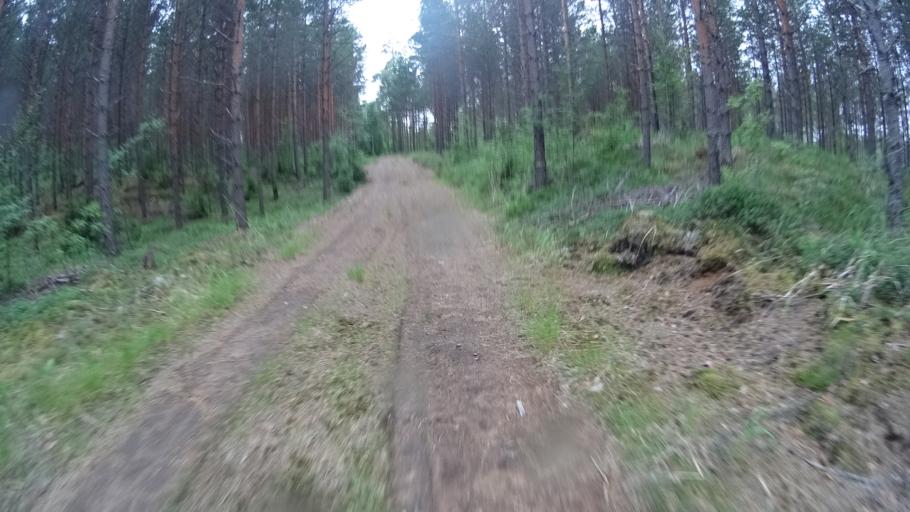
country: FI
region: Uusimaa
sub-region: Helsinki
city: Karkkila
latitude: 60.5937
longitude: 24.1770
